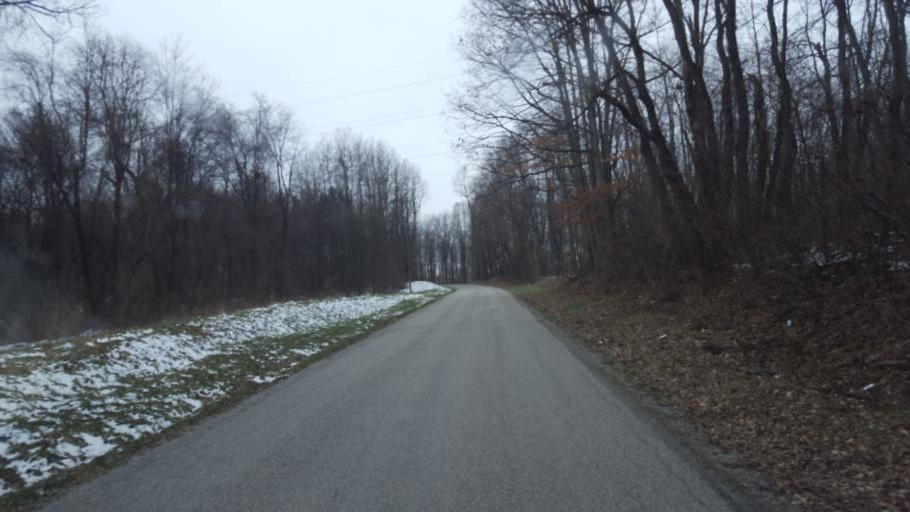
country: US
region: Ohio
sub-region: Sandusky County
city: Bellville
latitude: 40.5849
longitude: -82.4528
